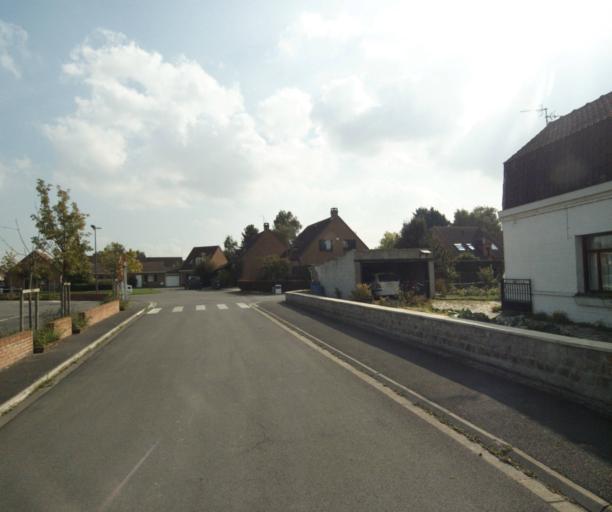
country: FR
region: Nord-Pas-de-Calais
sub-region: Departement du Nord
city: Houplin-Ancoisne
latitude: 50.5719
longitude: 2.9841
